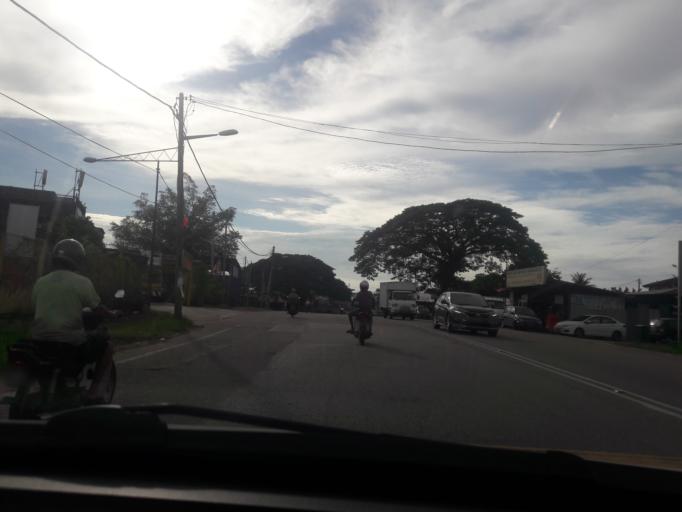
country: MY
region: Kedah
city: Sungai Petani
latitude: 5.6355
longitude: 100.4992
